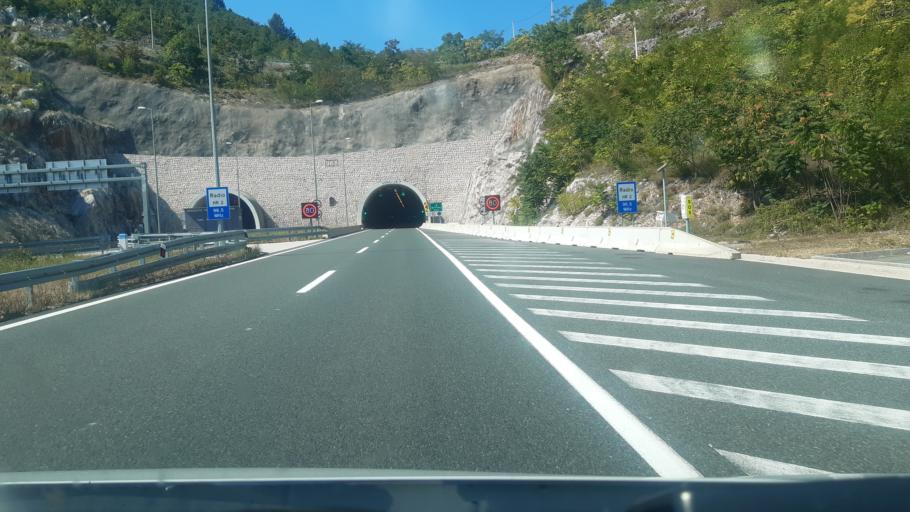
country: BA
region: Federation of Bosnia and Herzegovina
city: Ljubuski
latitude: 43.1447
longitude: 17.4888
